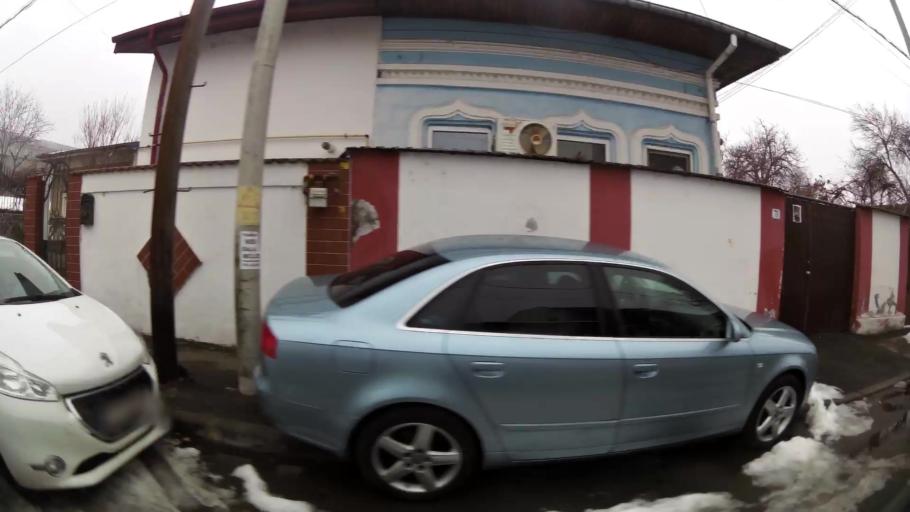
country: RO
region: Ilfov
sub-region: Comuna Chiajna
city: Rosu
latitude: 44.4608
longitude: 26.0497
